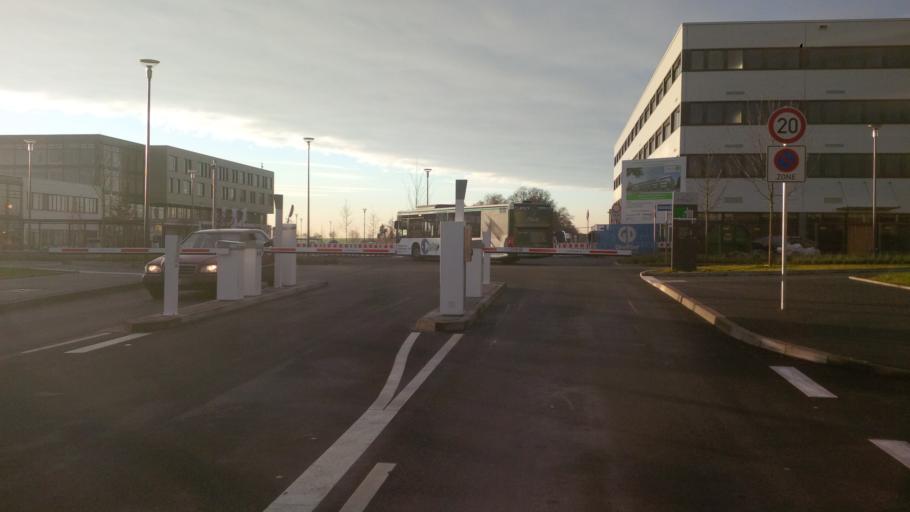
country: DE
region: Hesse
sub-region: Regierungsbezirk Darmstadt
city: Bad Homburg vor der Hoehe
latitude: 50.2135
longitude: 8.6177
